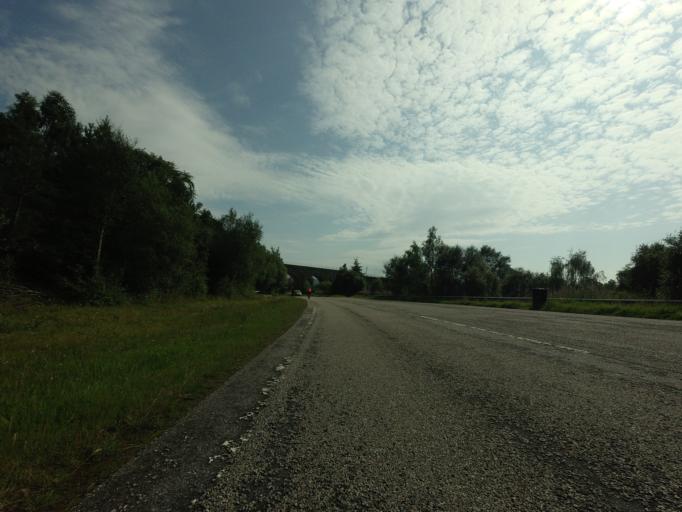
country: GB
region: Scotland
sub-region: Highland
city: Evanton
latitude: 57.9252
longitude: -4.4008
